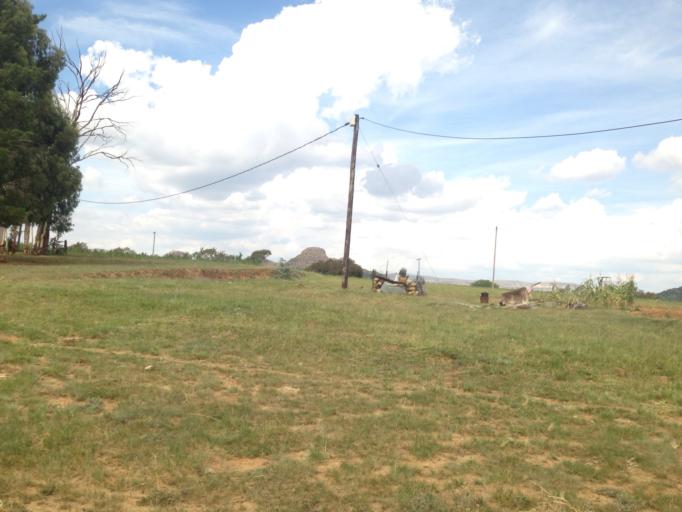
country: LS
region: Mafeteng
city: Mafeteng
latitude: -29.6967
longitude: 27.4302
